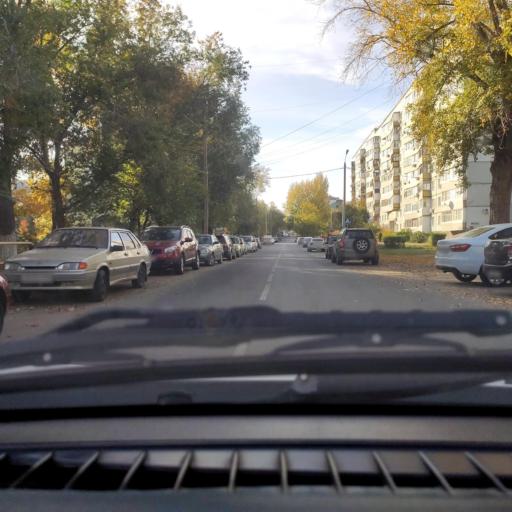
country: RU
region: Samara
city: Zhigulevsk
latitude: 53.4762
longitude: 49.4797
